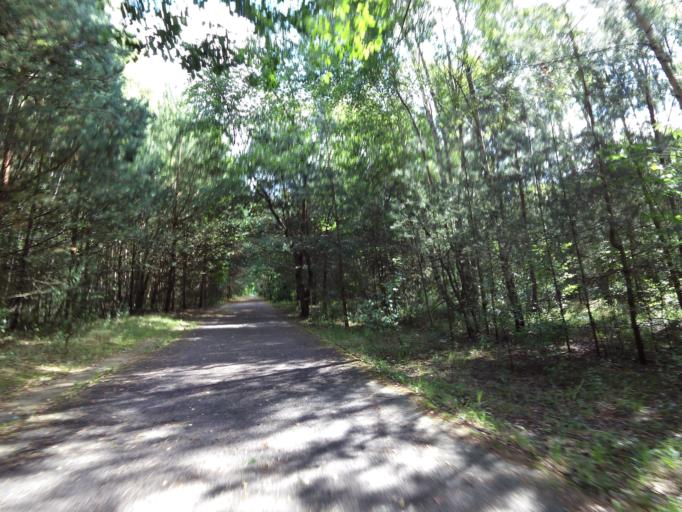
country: DE
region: Berlin
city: Lichtenrade
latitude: 52.3775
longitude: 13.3886
